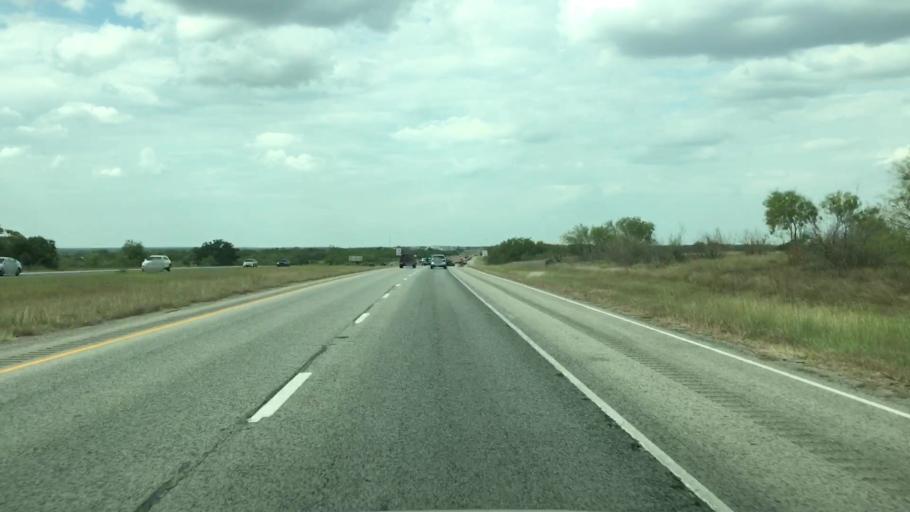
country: US
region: Texas
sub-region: Atascosa County
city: Pleasanton
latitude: 29.0638
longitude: -98.4327
